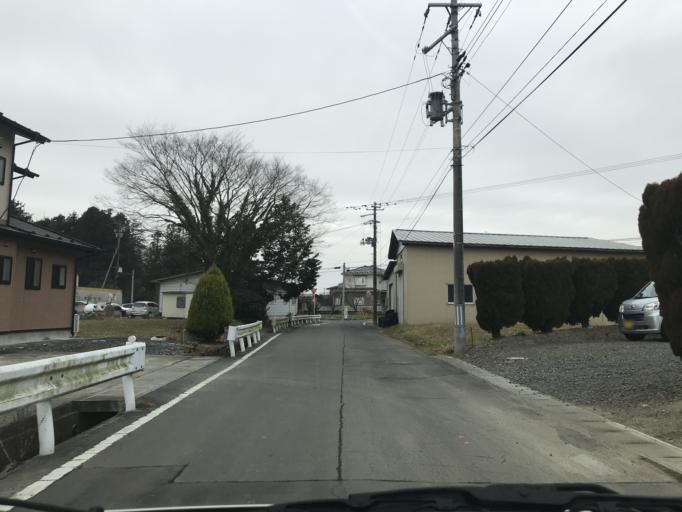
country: JP
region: Miyagi
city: Wakuya
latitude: 38.7225
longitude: 141.2148
